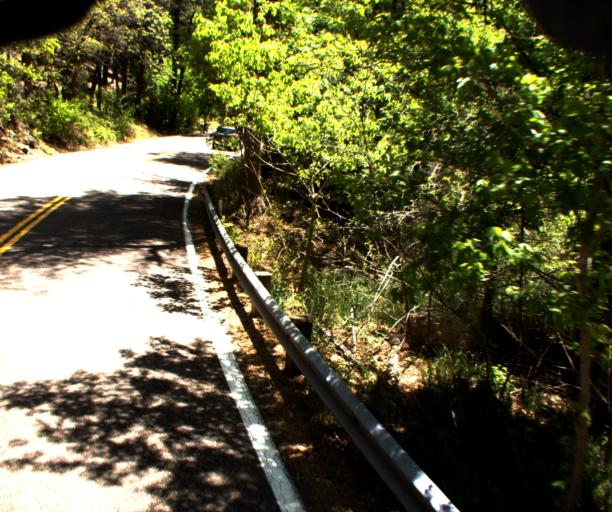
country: US
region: Arizona
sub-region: Coconino County
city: Kachina Village
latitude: 34.9925
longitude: -111.7360
